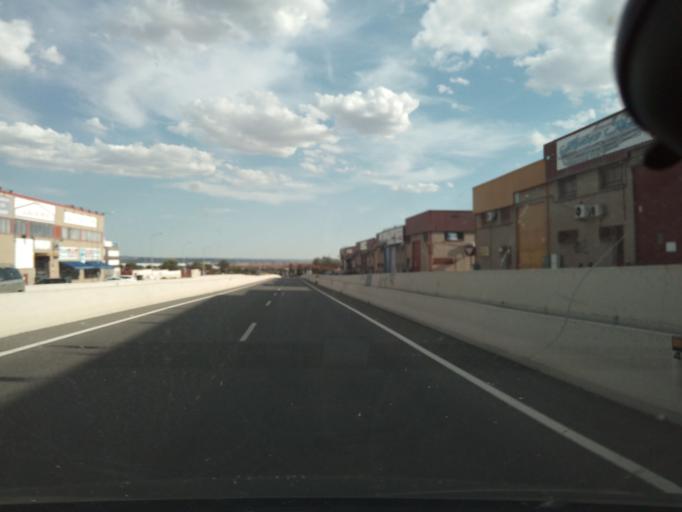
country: ES
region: Madrid
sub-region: Provincia de Madrid
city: Ajalvir
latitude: 40.5096
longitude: -3.4803
